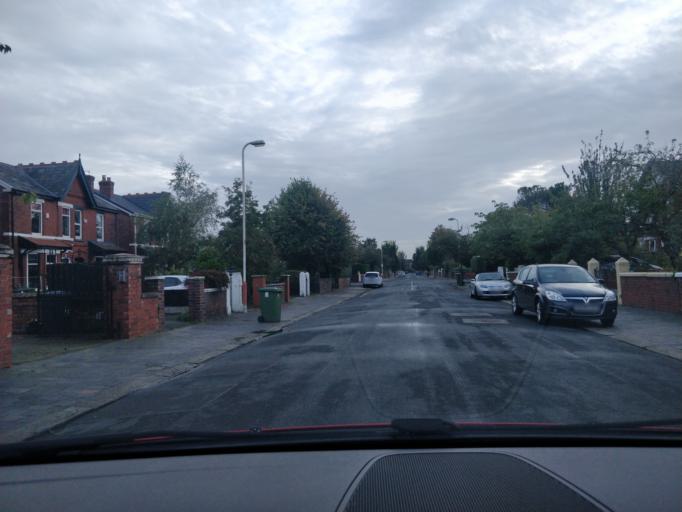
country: GB
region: England
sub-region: Sefton
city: Southport
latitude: 53.6423
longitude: -2.9863
